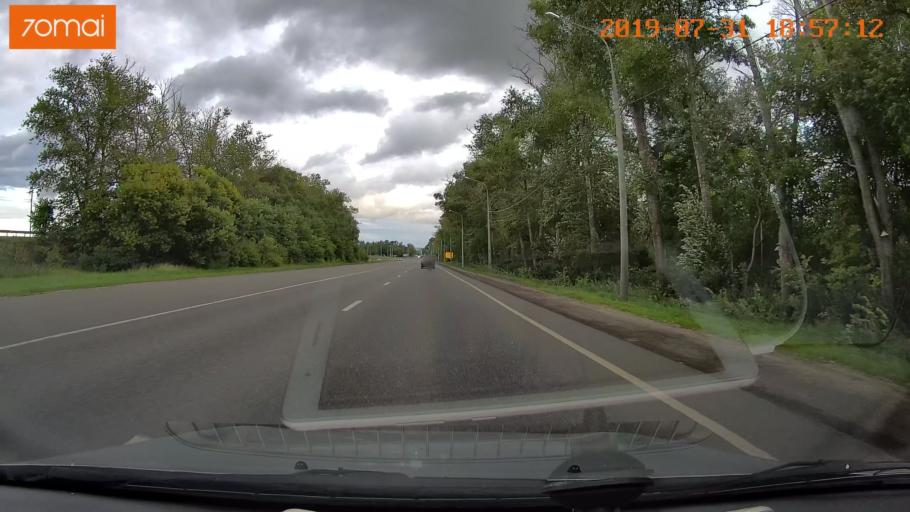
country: RU
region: Moskovskaya
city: Raduzhnyy
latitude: 55.1561
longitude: 38.6890
